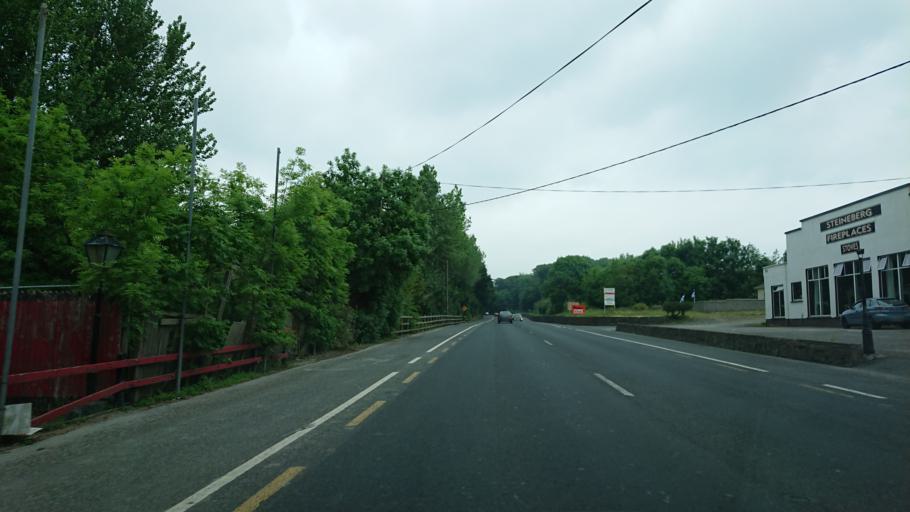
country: IE
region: Munster
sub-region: Waterford
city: Waterford
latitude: 52.2064
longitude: -7.1162
